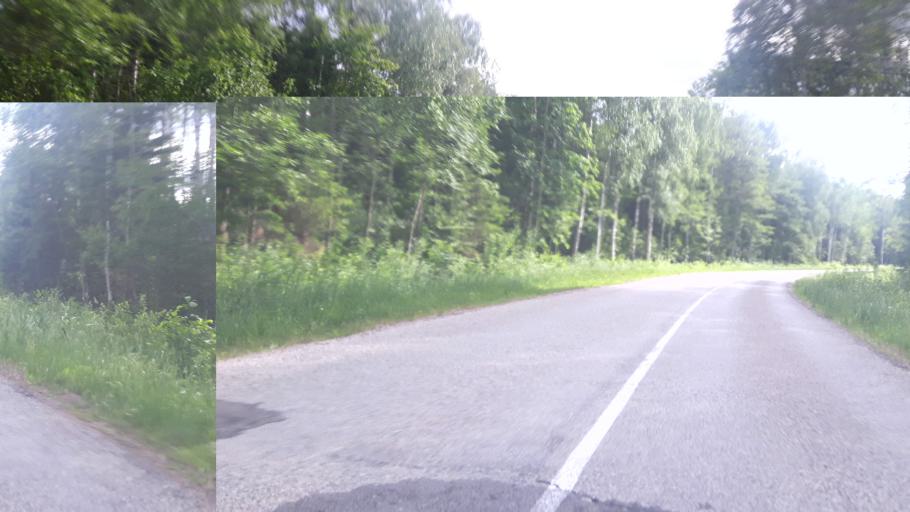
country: LV
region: Engure
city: Smarde
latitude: 57.0269
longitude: 23.3573
